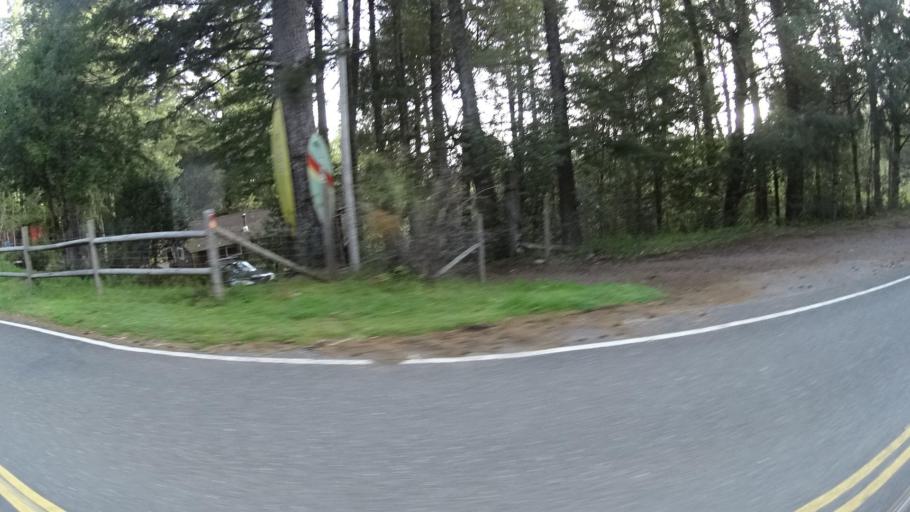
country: US
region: California
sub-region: Humboldt County
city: Bayside
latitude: 40.7450
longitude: -123.9640
